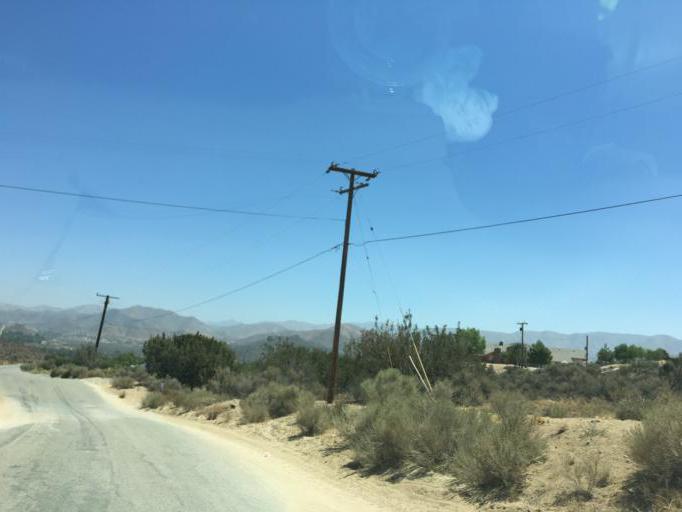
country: US
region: California
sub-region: Los Angeles County
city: Acton
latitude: 34.4733
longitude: -118.2111
